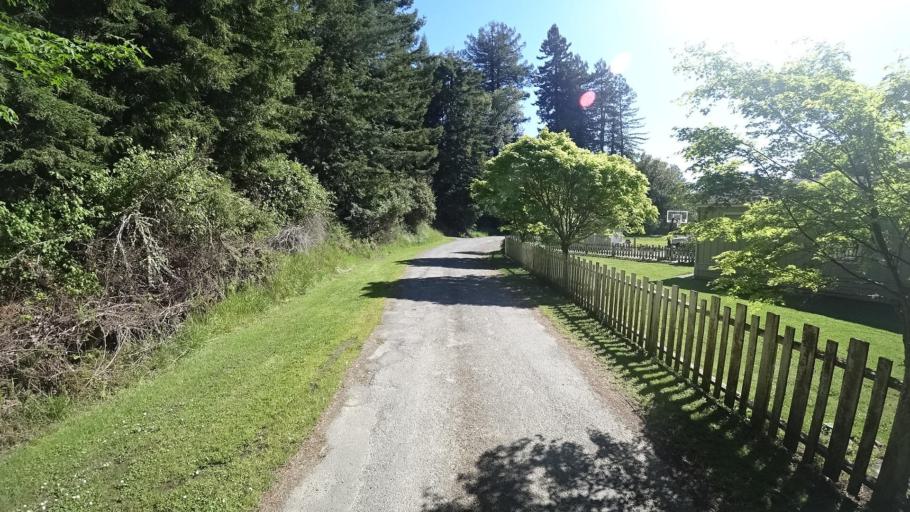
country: US
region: California
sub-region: Humboldt County
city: Rio Dell
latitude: 40.5290
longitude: -124.1693
